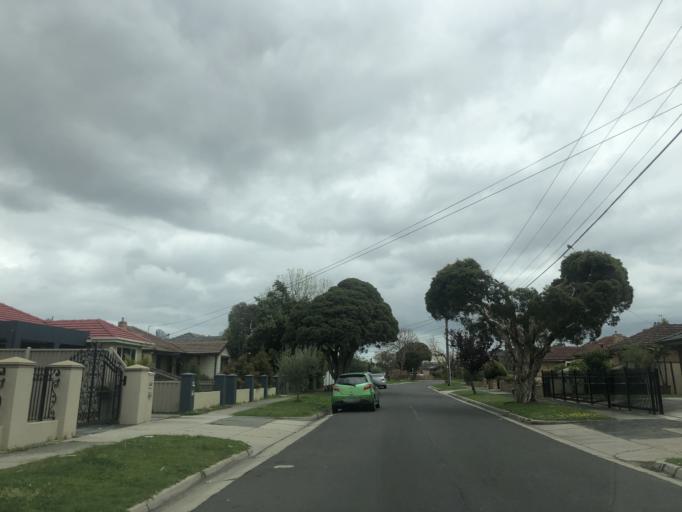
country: AU
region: Victoria
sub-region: Greater Dandenong
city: Dandenong North
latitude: -37.9746
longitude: 145.2120
